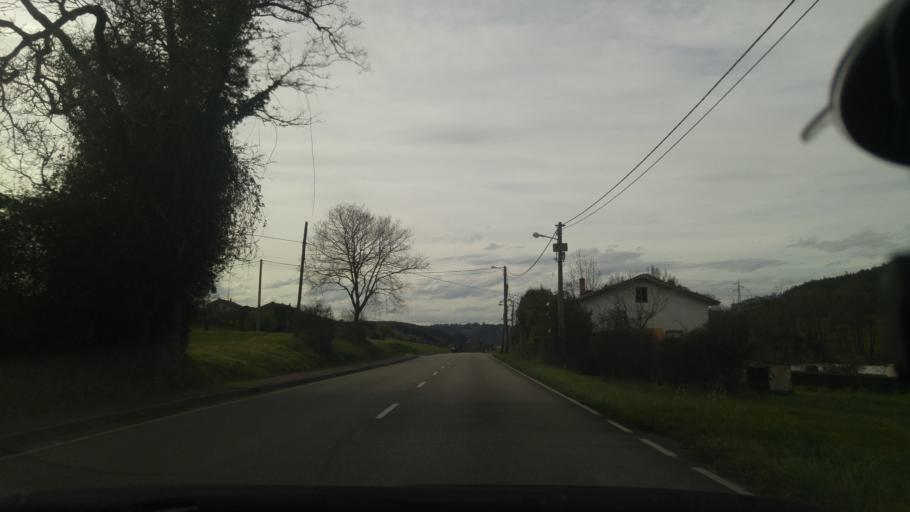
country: ES
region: Asturias
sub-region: Province of Asturias
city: Corvera de Asturias
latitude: 43.4890
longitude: -5.8465
